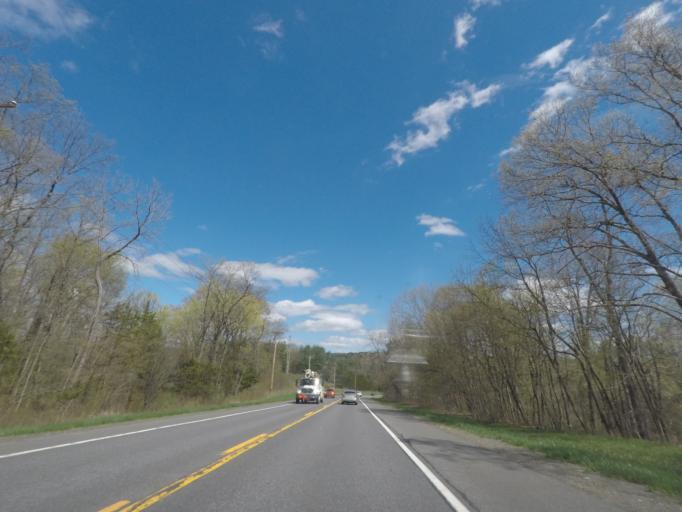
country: US
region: New York
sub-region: Columbia County
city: Hudson
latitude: 42.2188
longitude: -73.8061
